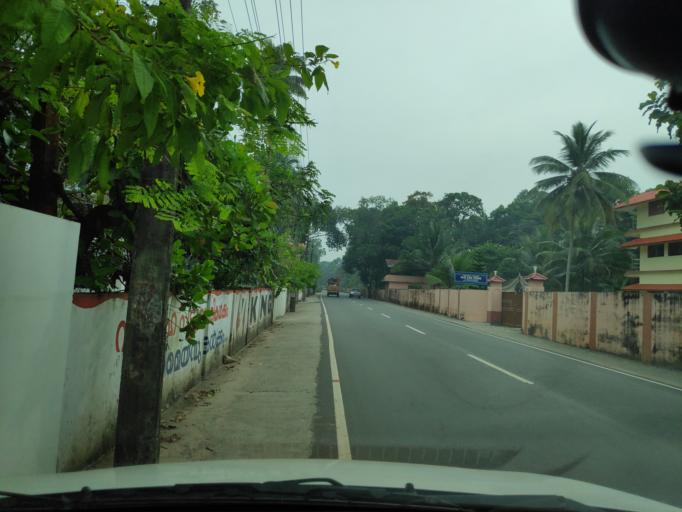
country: IN
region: Kerala
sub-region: Alappuzha
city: Shertallai
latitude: 9.6085
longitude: 76.3376
